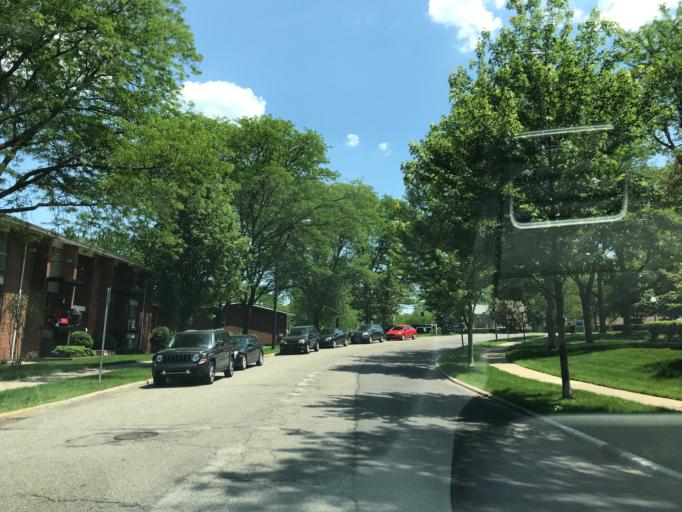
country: US
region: Michigan
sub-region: Washtenaw County
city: Ann Arbor
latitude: 42.2587
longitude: -83.7155
